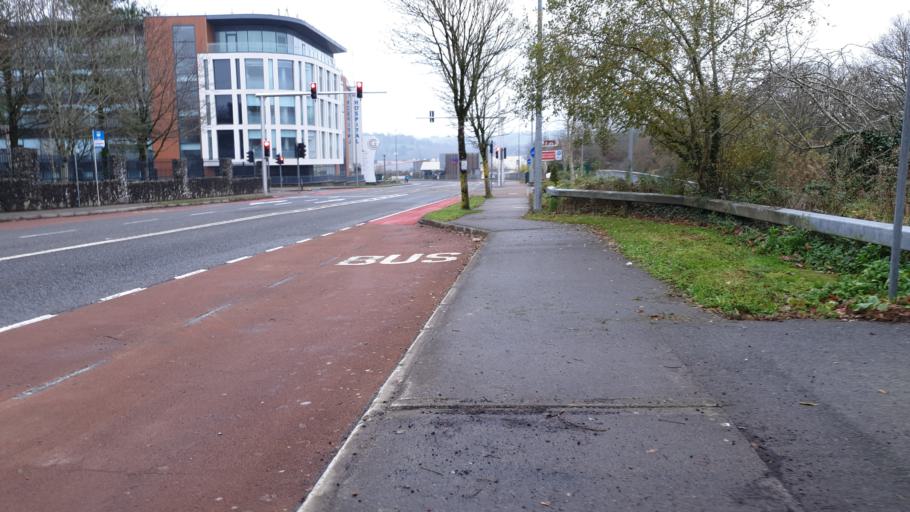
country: IE
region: Munster
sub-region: County Cork
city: Cork
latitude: 51.8867
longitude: -8.4074
